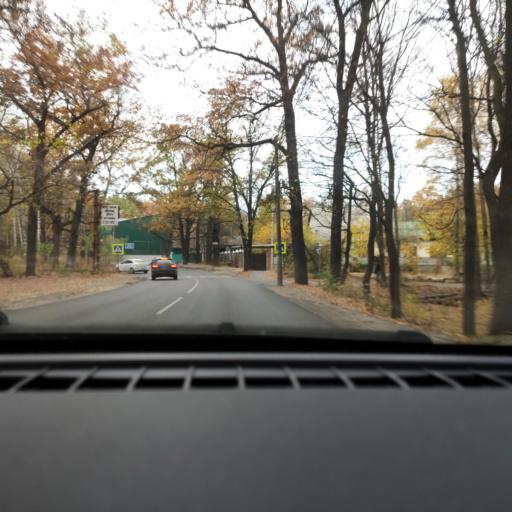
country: RU
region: Voronezj
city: Voronezh
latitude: 51.7225
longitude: 39.2221
